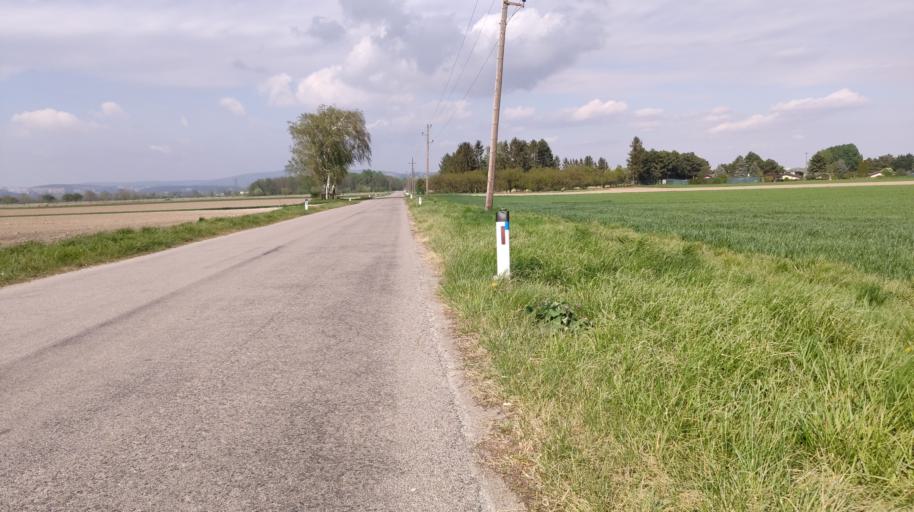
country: AT
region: Lower Austria
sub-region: Politischer Bezirk Bruck an der Leitha
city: Berg
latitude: 48.1095
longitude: 17.0513
